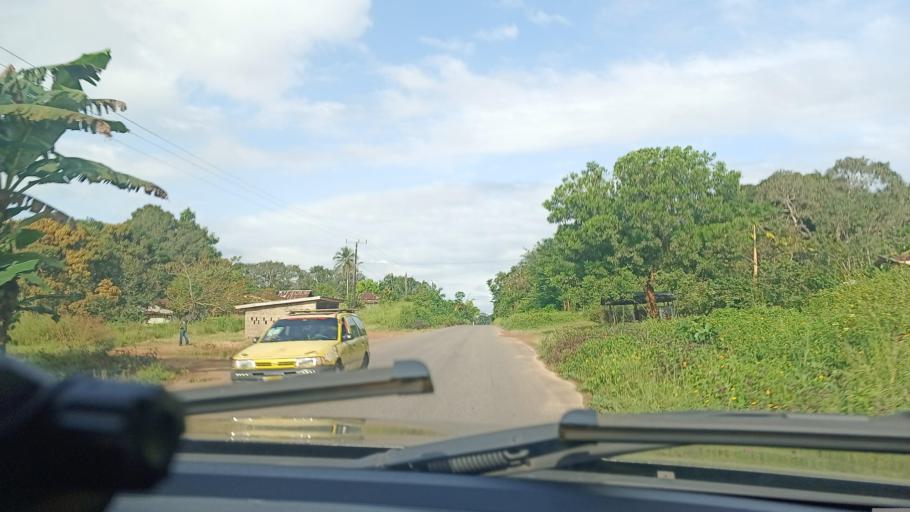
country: LR
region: Bomi
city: Tubmanburg
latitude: 6.6960
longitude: -10.9035
